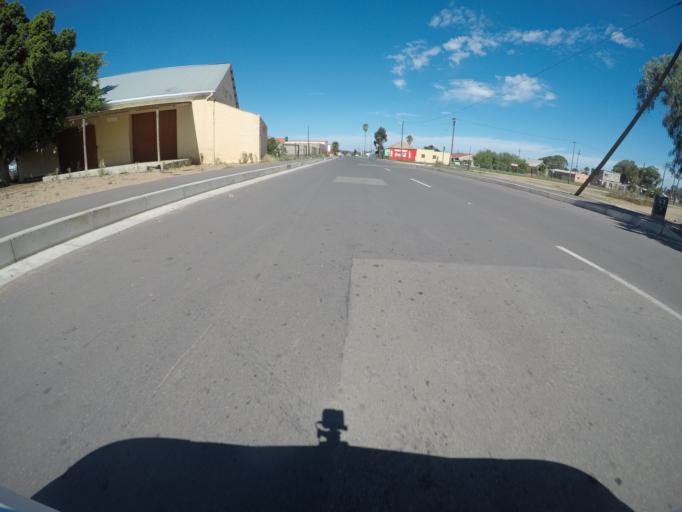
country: ZA
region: Western Cape
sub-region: West Coast District Municipality
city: Malmesbury
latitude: -33.5726
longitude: 18.6470
